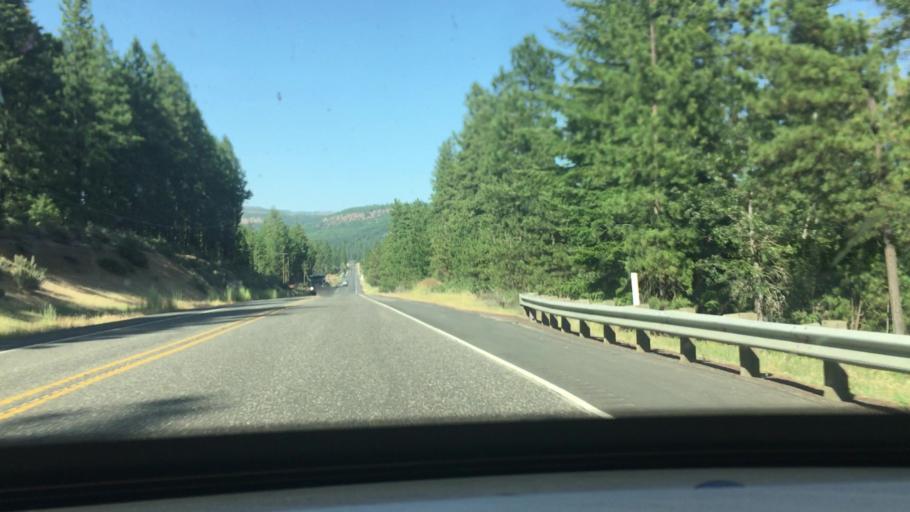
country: US
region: Washington
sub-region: Klickitat County
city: Goldendale
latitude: 45.9368
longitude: -120.6888
